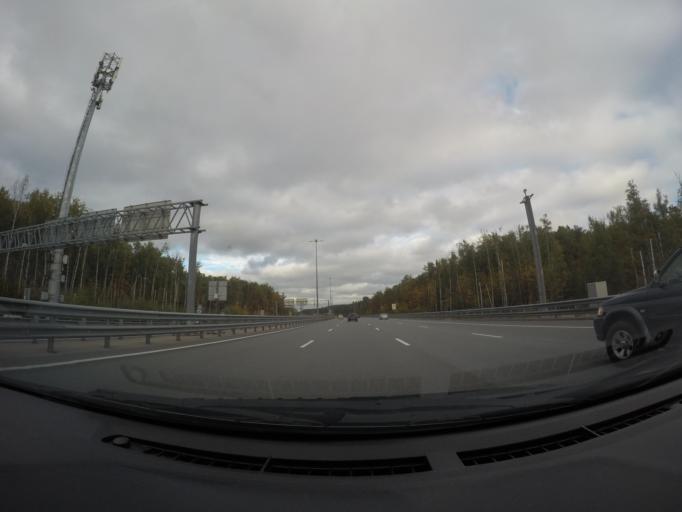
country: RU
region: Moskovskaya
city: Odintsovo
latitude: 55.6993
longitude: 37.2977
